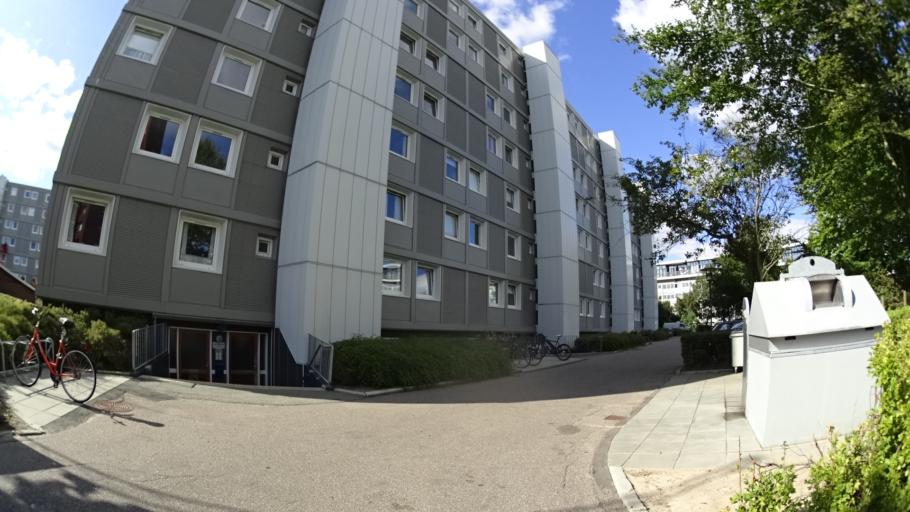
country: DK
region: Central Jutland
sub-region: Arhus Kommune
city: Arhus
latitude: 56.1425
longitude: 10.1848
